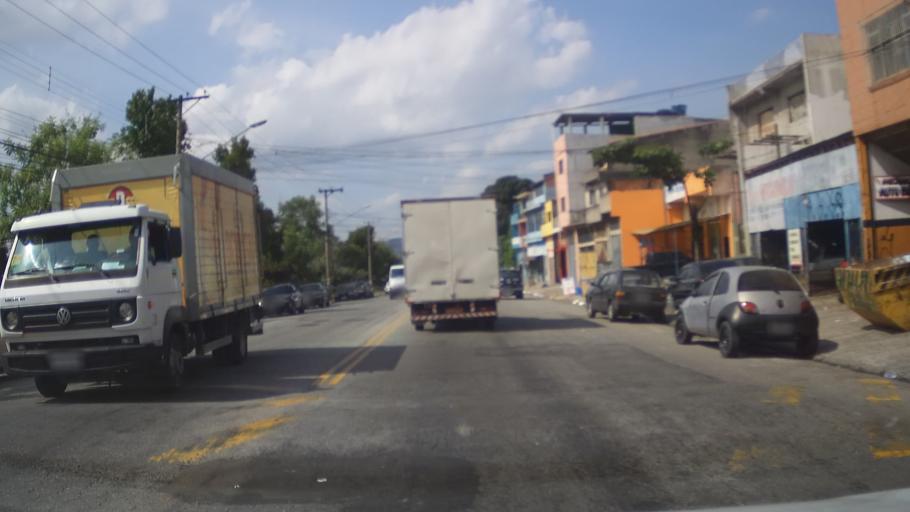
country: BR
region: Sao Paulo
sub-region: Guarulhos
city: Guarulhos
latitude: -23.4413
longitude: -46.4689
